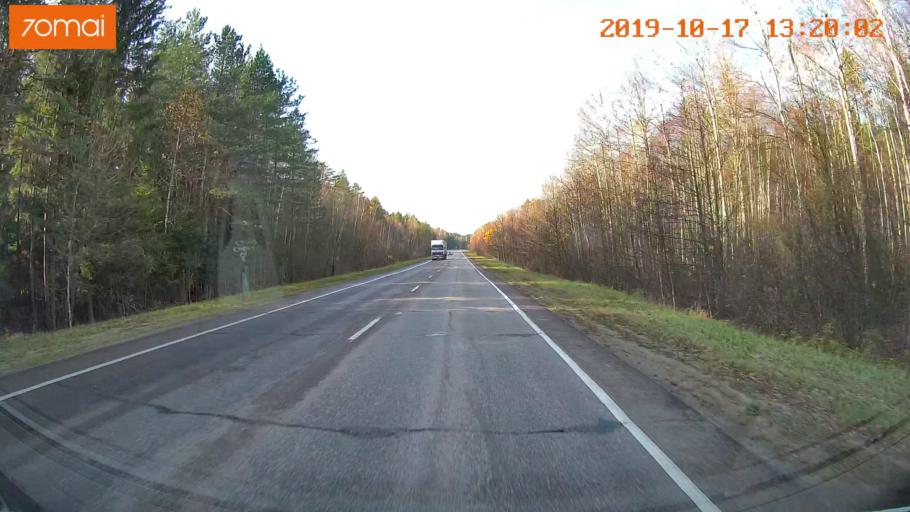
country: RU
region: Rjazan
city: Gus'-Zheleznyy
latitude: 55.0733
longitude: 41.0597
